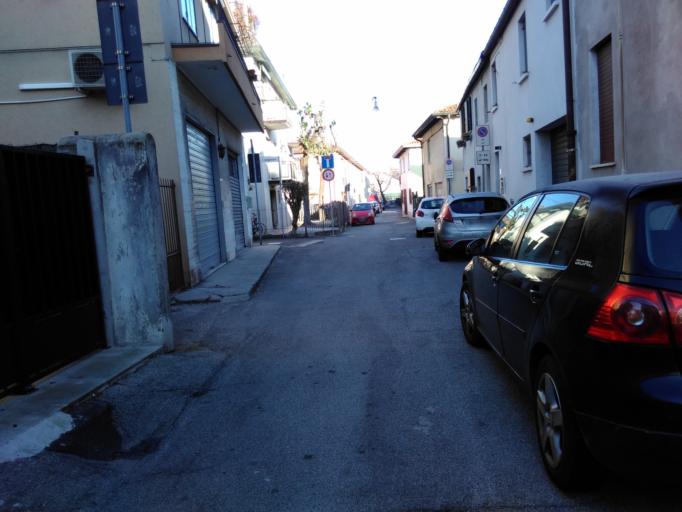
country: IT
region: Veneto
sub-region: Provincia di Venezia
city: Mestre
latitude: 45.4935
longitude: 12.2342
